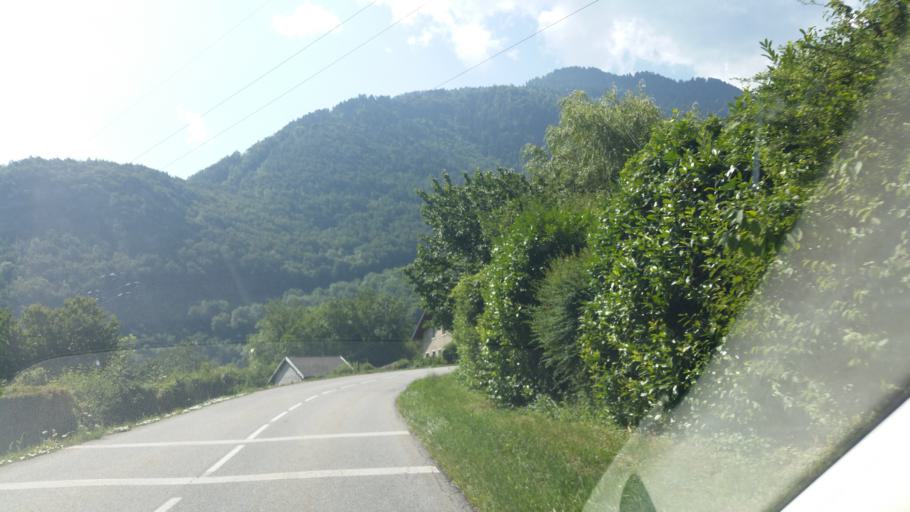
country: FR
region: Rhone-Alpes
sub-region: Departement de la Savoie
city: Aigueblanche
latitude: 45.4988
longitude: 6.5053
